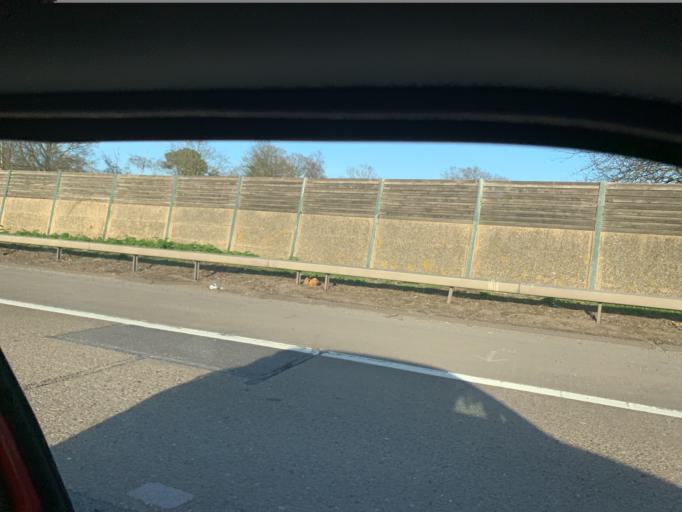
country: GB
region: England
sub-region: Surrey
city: Addlestone
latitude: 51.3603
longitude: -0.4970
